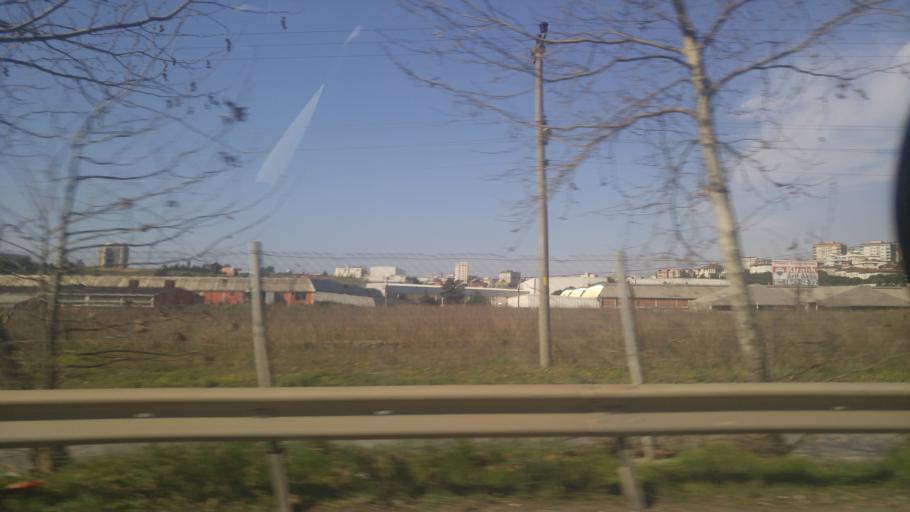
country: TR
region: Kocaeli
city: Darica
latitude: 40.8235
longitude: 29.3646
